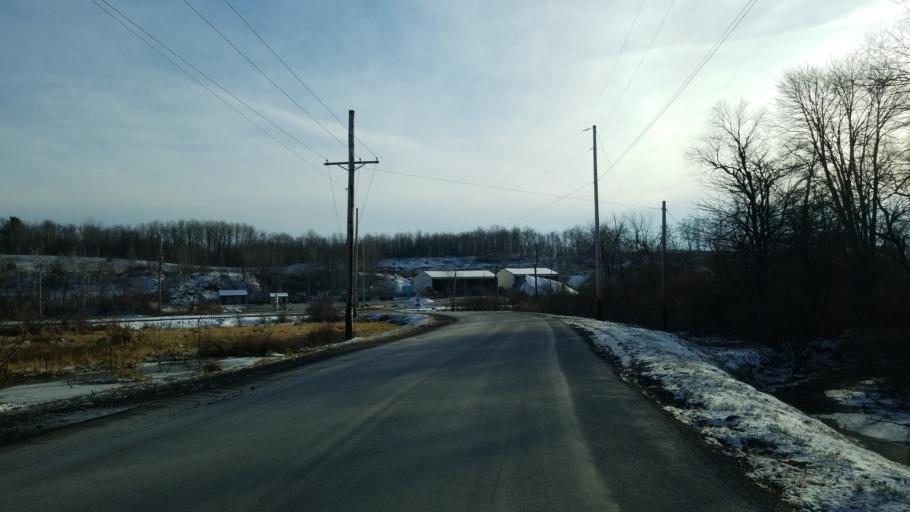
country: US
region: Pennsylvania
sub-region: Clearfield County
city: DuBois
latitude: 41.1219
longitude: -78.7169
